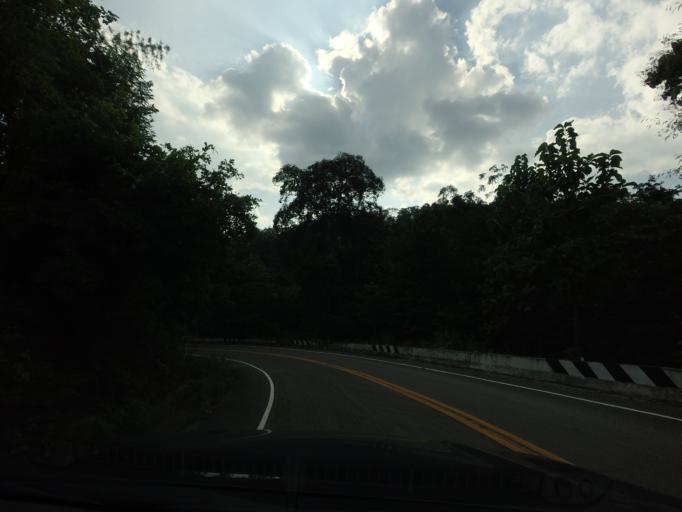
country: TH
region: Nan
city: Na Noi
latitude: 18.2915
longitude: 100.9163
